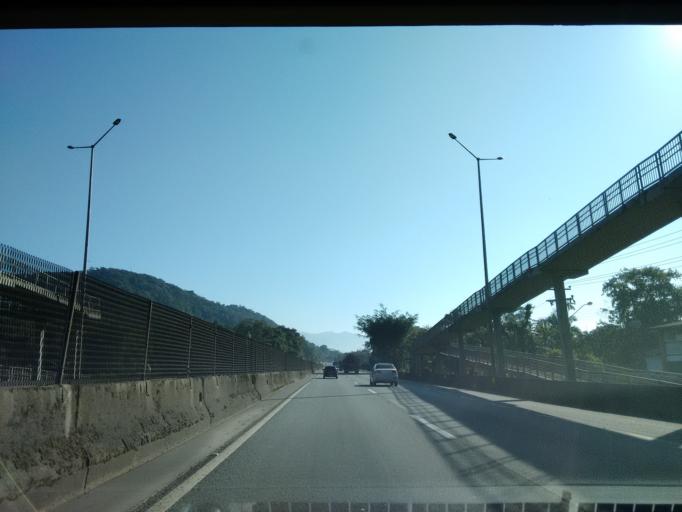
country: BR
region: Santa Catarina
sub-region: Joinville
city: Joinville
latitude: -26.2184
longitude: -48.9161
